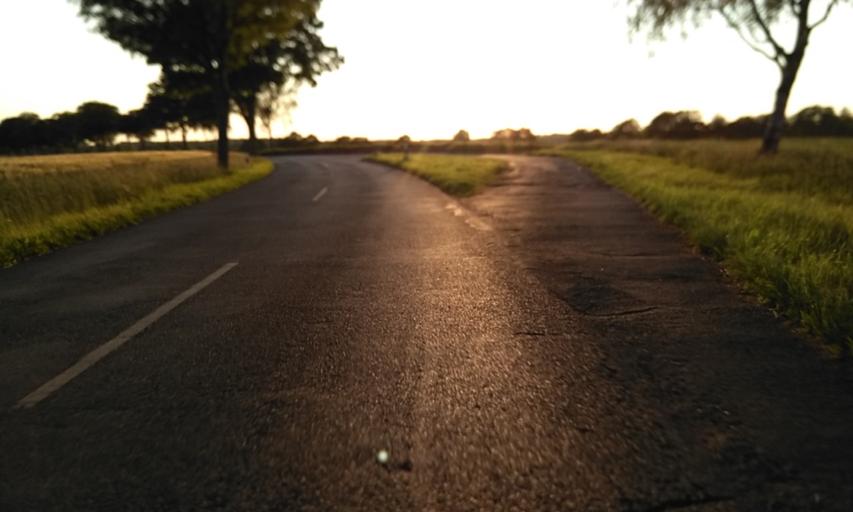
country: DE
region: Lower Saxony
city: Ahlerstedt
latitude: 53.4274
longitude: 9.4456
